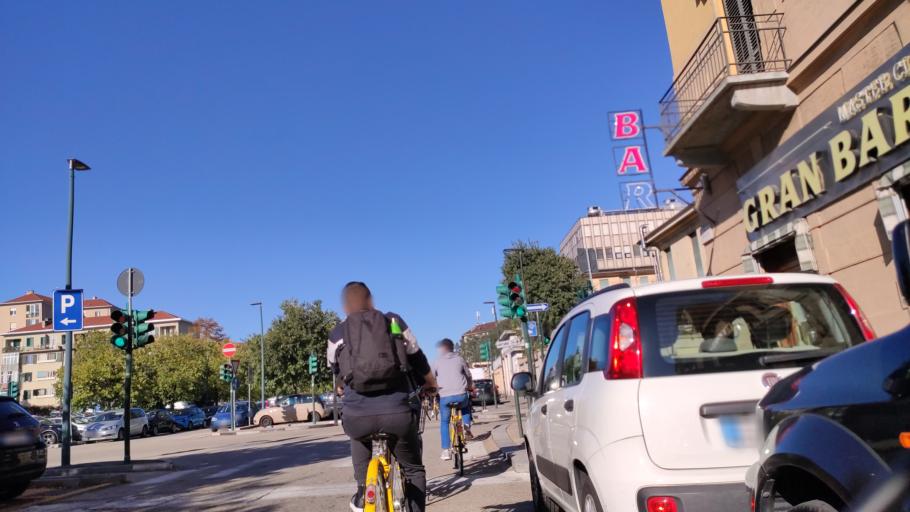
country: IT
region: Piedmont
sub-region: Provincia di Torino
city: Turin
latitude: 45.0367
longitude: 7.6739
